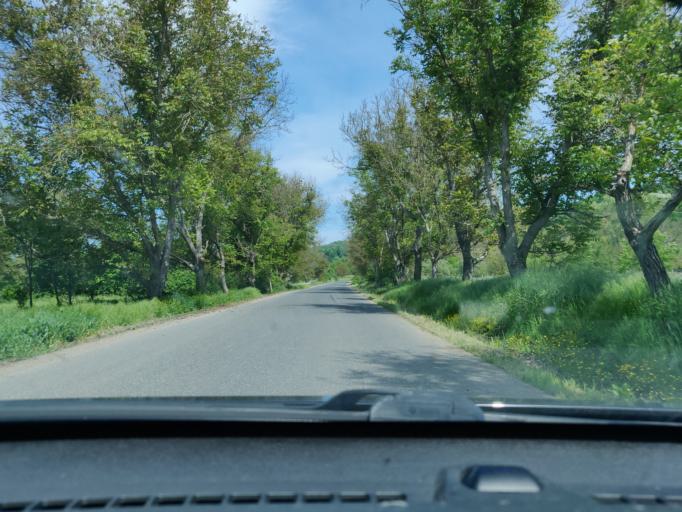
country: RO
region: Vrancea
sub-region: Comuna Vidra
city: Vidra
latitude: 45.9431
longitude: 26.8748
